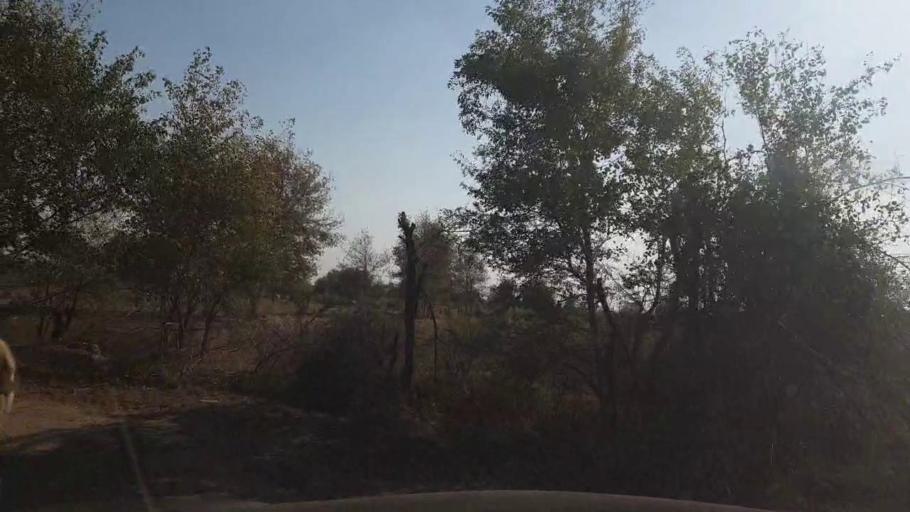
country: PK
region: Sindh
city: Mirpur Mathelo
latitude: 27.9952
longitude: 69.4841
